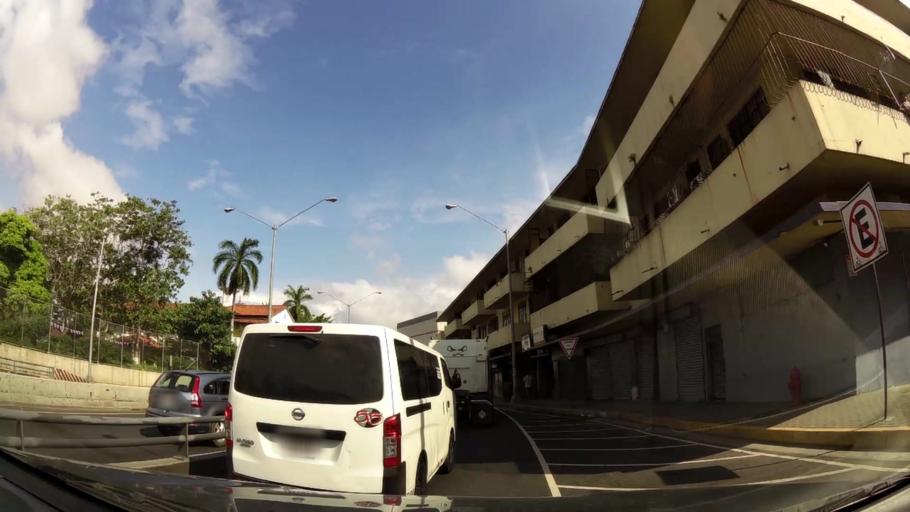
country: PA
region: Panama
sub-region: Distrito de Panama
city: Ancon
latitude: 8.9603
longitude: -79.5427
